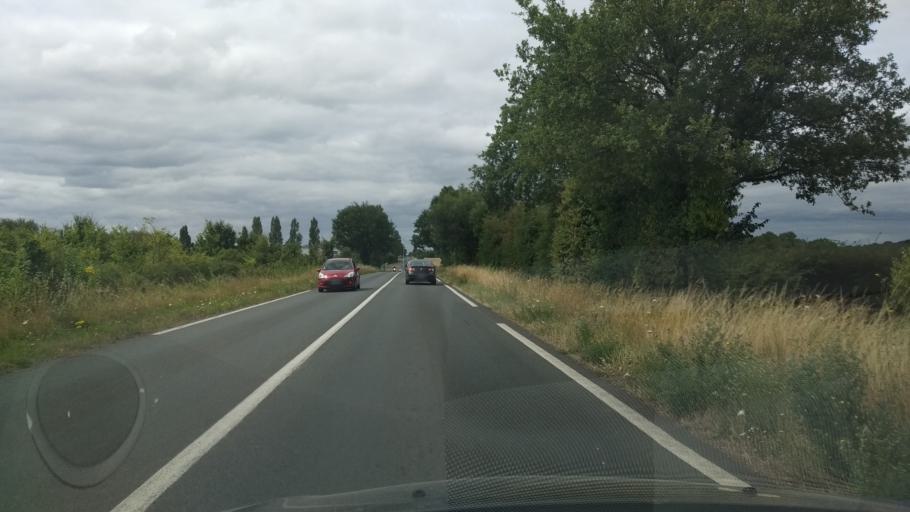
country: FR
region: Poitou-Charentes
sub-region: Departement de la Vienne
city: Smarves
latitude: 46.5026
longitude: 0.3630
